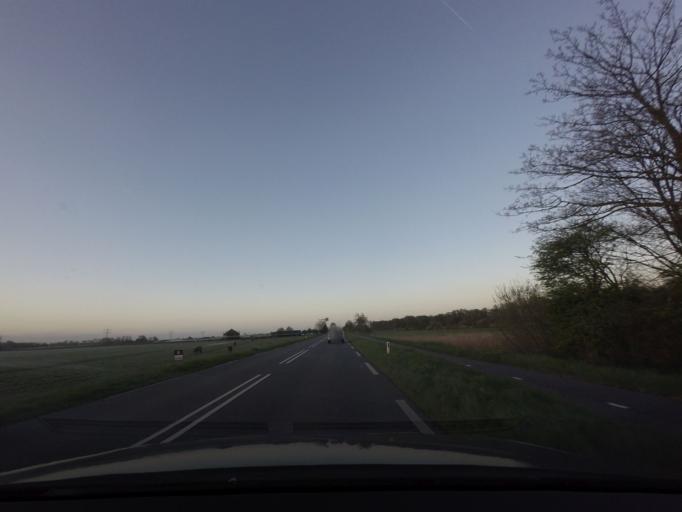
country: NL
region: North Holland
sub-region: Gemeente Uitgeest
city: Uitgeest
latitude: 52.5528
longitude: 4.7803
